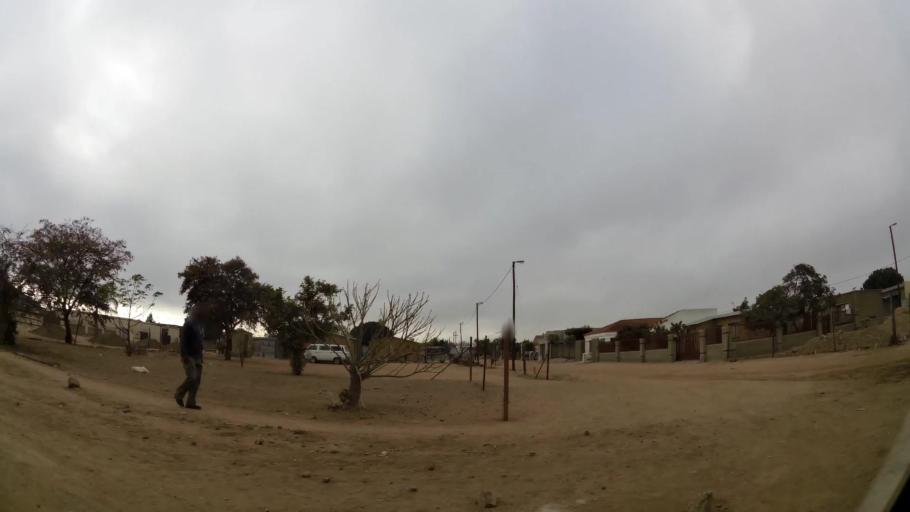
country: ZA
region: Limpopo
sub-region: Capricorn District Municipality
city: Polokwane
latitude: -23.8336
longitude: 29.3897
